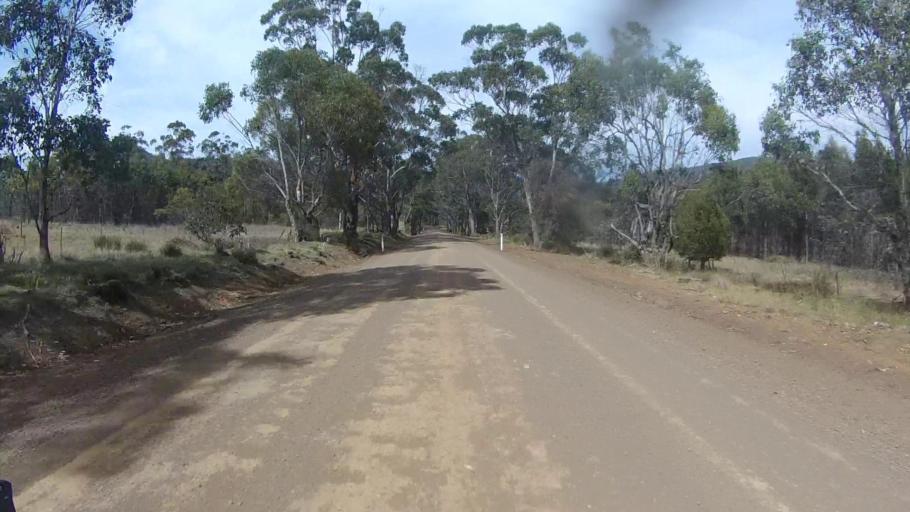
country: AU
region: Tasmania
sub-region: Sorell
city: Sorell
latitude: -42.6613
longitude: 147.8938
